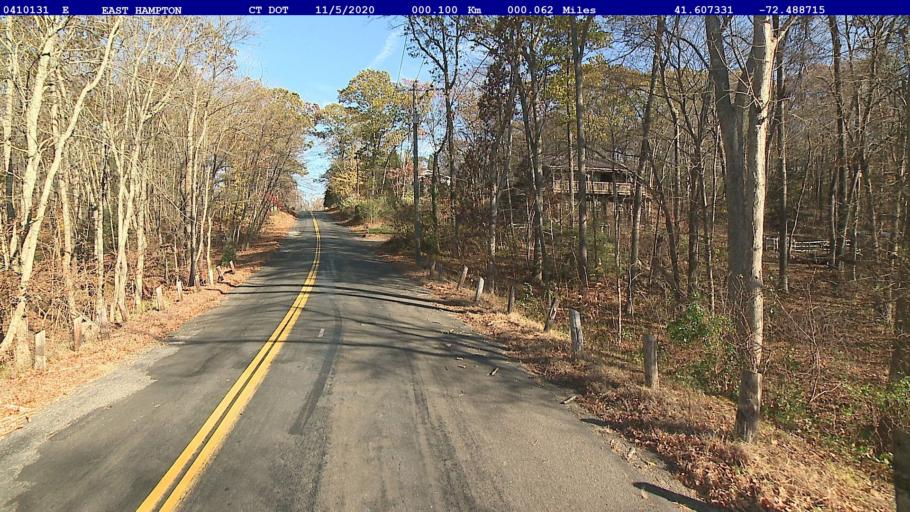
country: US
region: Connecticut
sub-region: Middlesex County
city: Lake Pocotopaug
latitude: 41.6074
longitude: -72.4887
